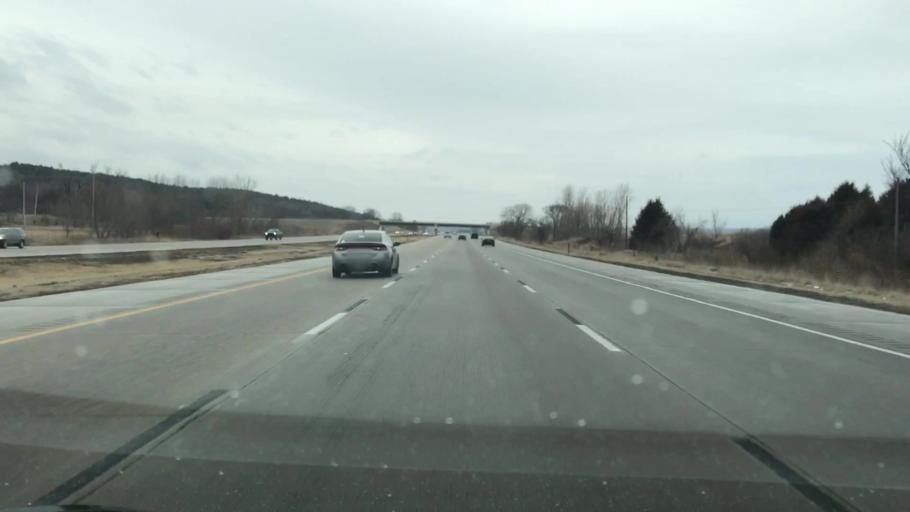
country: US
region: Nebraska
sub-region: Sarpy County
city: Gretna
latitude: 41.0760
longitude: -96.2820
